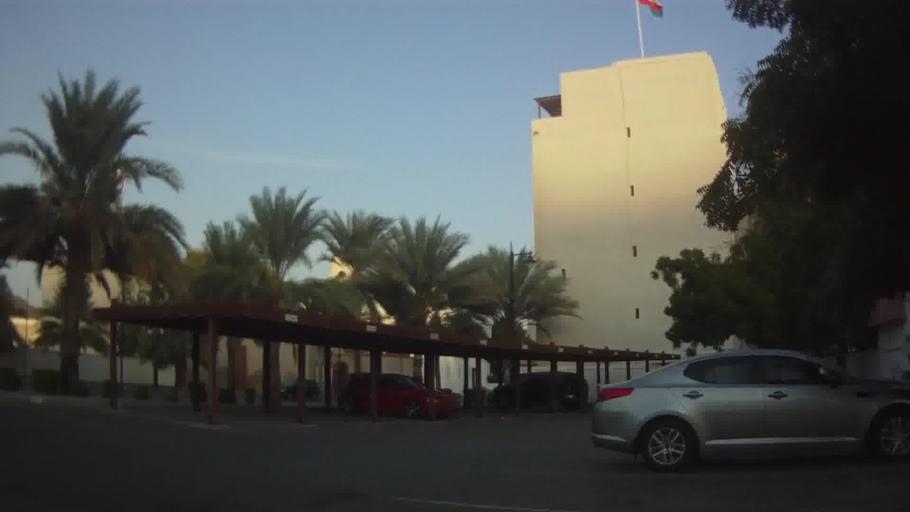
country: OM
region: Muhafazat Masqat
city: Muscat
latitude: 23.6155
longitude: 58.5896
